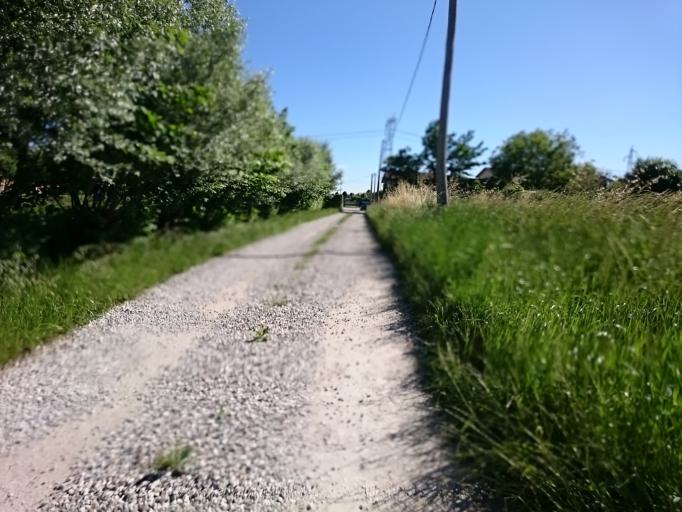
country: IT
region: Veneto
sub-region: Provincia di Padova
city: Saonara
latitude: 45.3597
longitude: 11.9745
